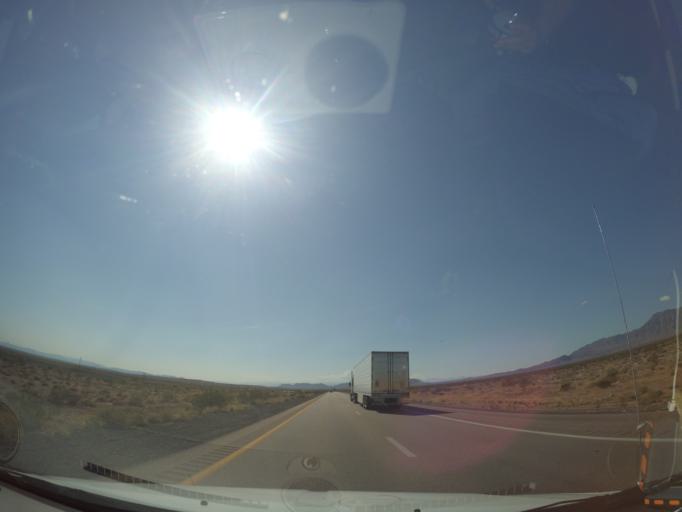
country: US
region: Nevada
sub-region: Clark County
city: Bunkerville
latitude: 36.7659
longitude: -114.3400
